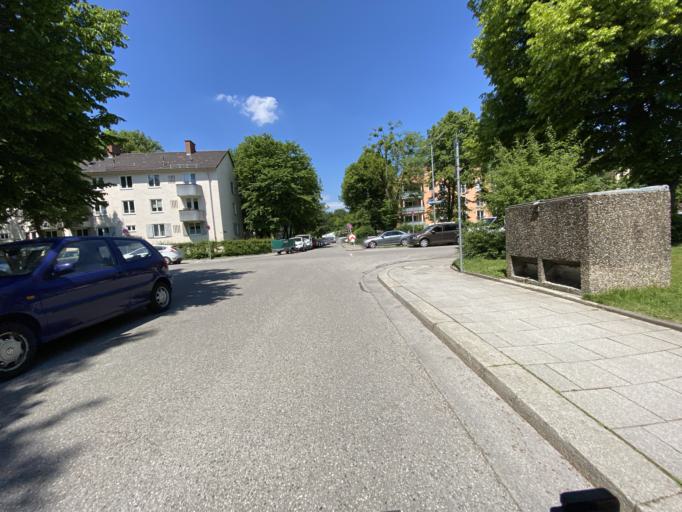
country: DE
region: Bavaria
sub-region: Upper Bavaria
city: Munich
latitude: 48.1203
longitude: 11.5270
